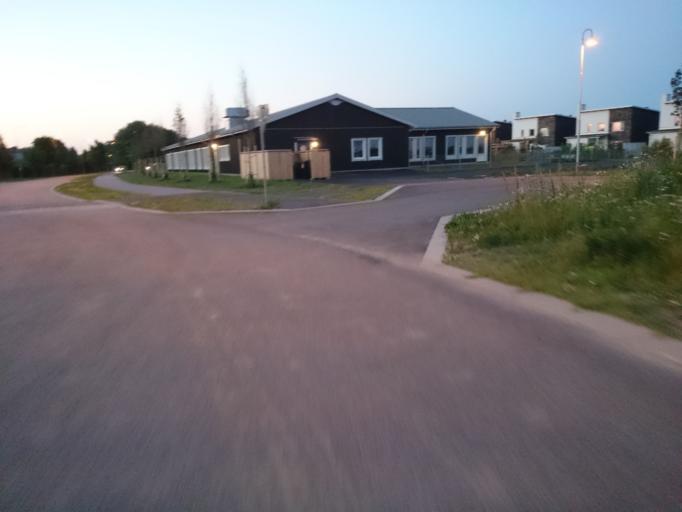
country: SE
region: Skane
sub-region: Staffanstorps Kommun
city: Hjaerup
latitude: 55.6723
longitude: 13.1465
